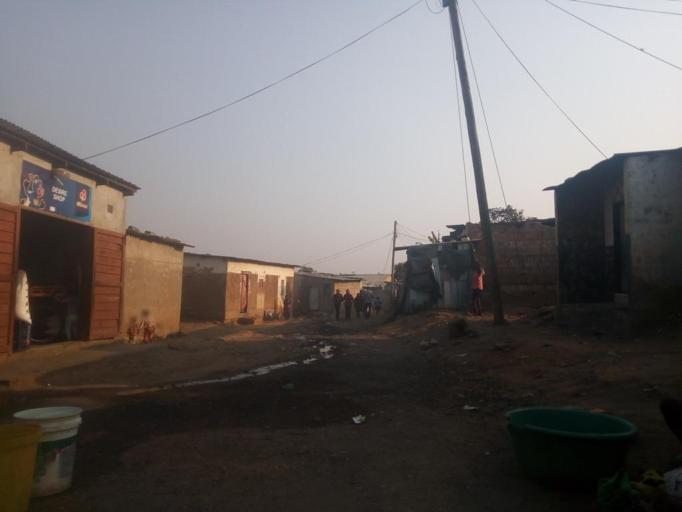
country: ZM
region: Lusaka
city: Lusaka
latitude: -15.4052
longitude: 28.3635
